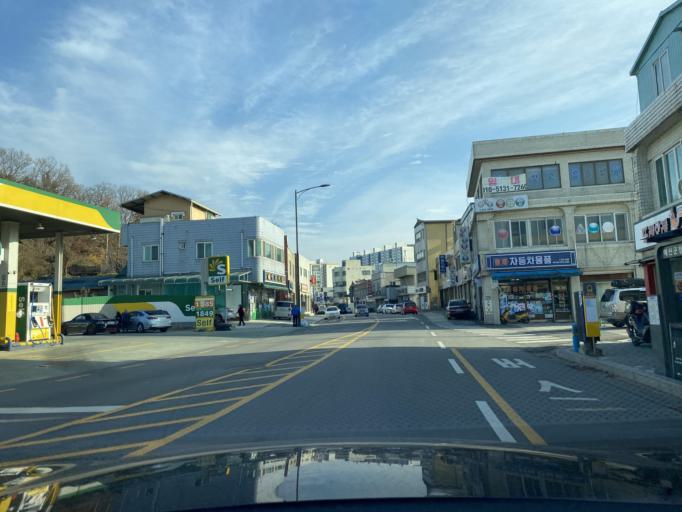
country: KR
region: Chungcheongnam-do
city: Yesan
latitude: 36.6813
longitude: 126.8332
